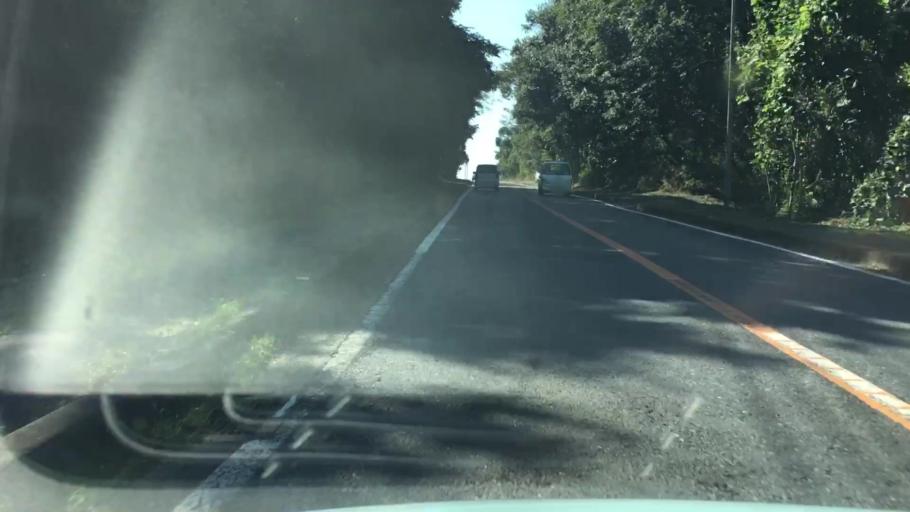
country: JP
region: Ibaraki
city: Ryugasaki
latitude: 35.8805
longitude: 140.1585
